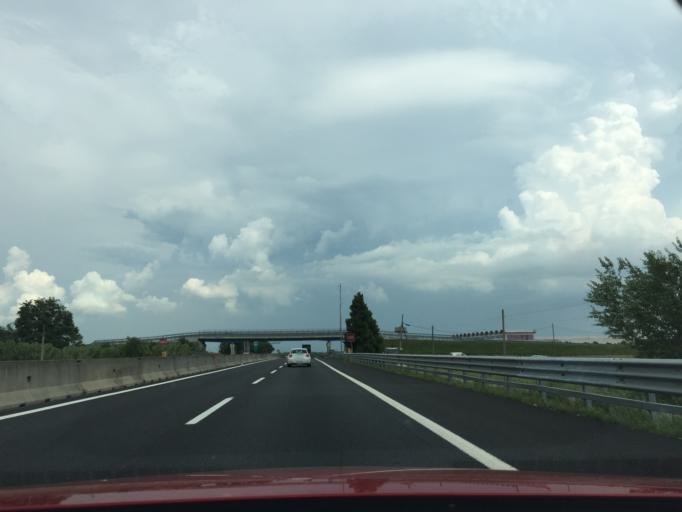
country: IT
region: Tuscany
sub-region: Provincia di Lucca
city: Porcari
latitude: 43.8197
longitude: 10.6217
